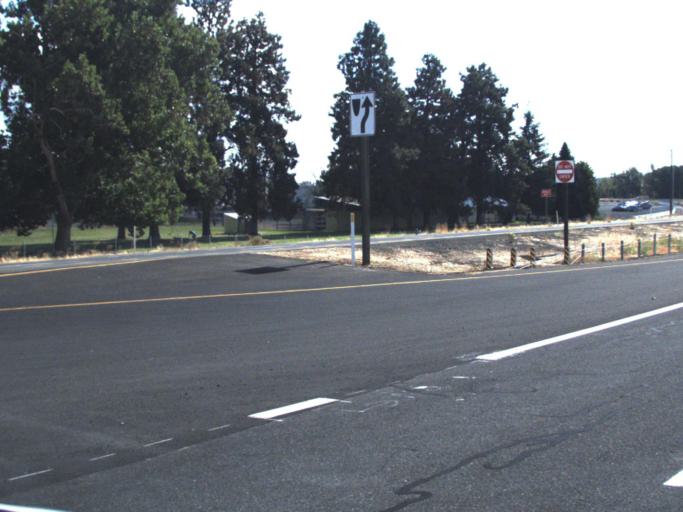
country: US
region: Washington
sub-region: Yakima County
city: Gleed
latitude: 46.6871
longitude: -120.6533
